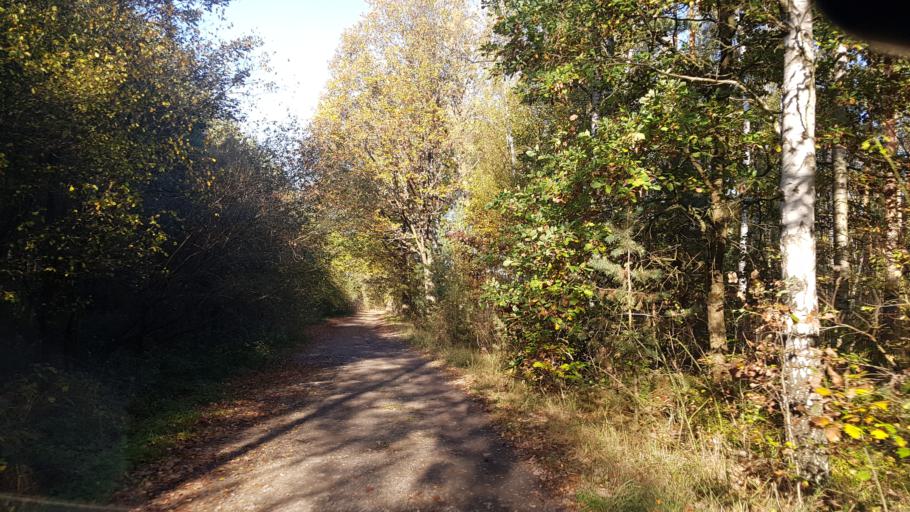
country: DE
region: Brandenburg
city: Ruckersdorf
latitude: 51.5498
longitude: 13.5368
